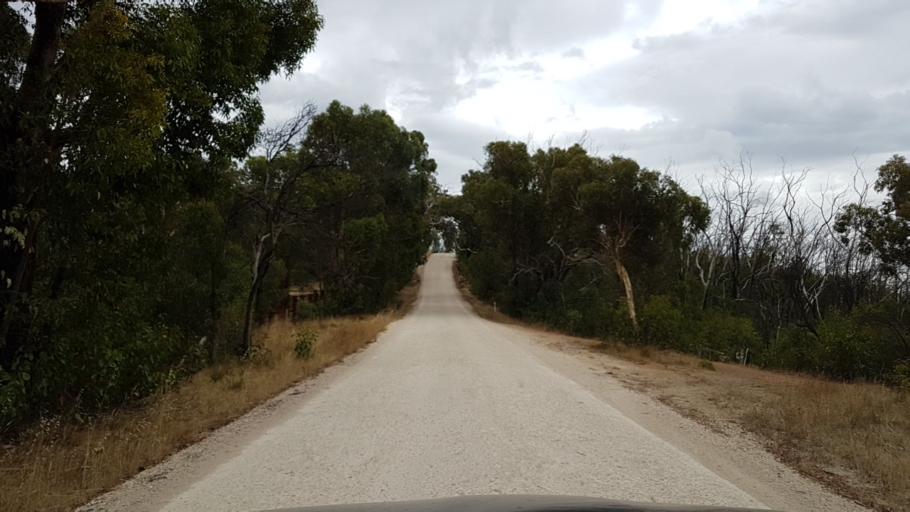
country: AU
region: South Australia
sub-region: Tea Tree Gully
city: Golden Grove
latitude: -34.7825
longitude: 138.8137
